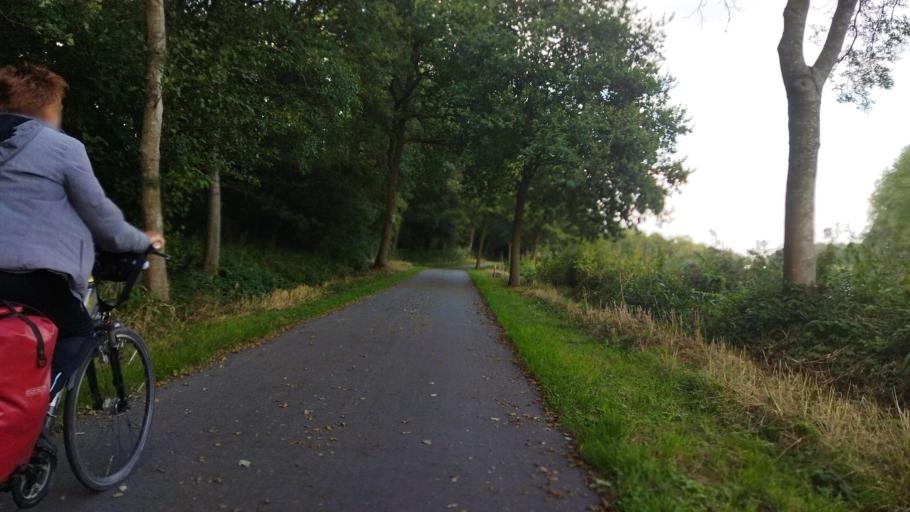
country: DE
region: Lower Saxony
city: Dersum
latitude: 52.9553
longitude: 7.2931
